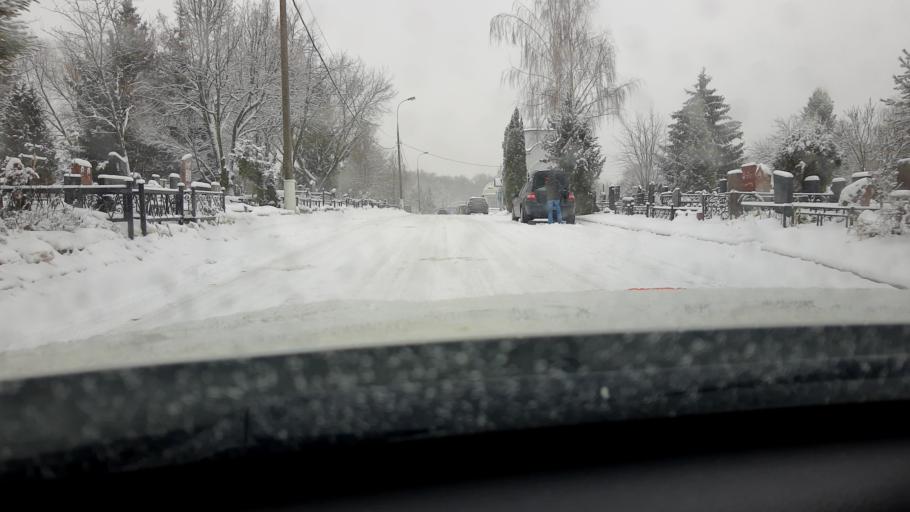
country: RU
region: Moskovskaya
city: Krasnogorsk
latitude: 55.8737
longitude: 37.3475
